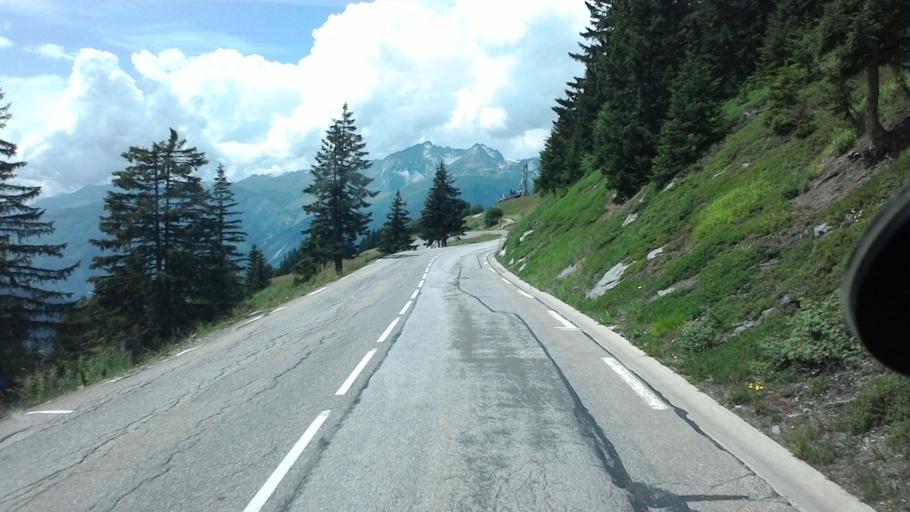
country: FR
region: Rhone-Alpes
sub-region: Departement de la Savoie
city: Seez
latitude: 45.6229
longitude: 6.8532
